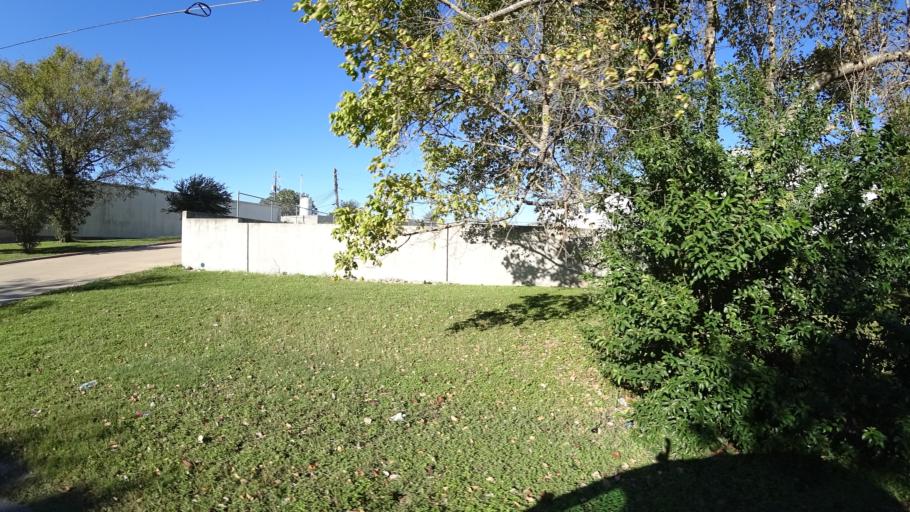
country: US
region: Texas
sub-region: Travis County
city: Manor
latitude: 30.3242
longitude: -97.6525
